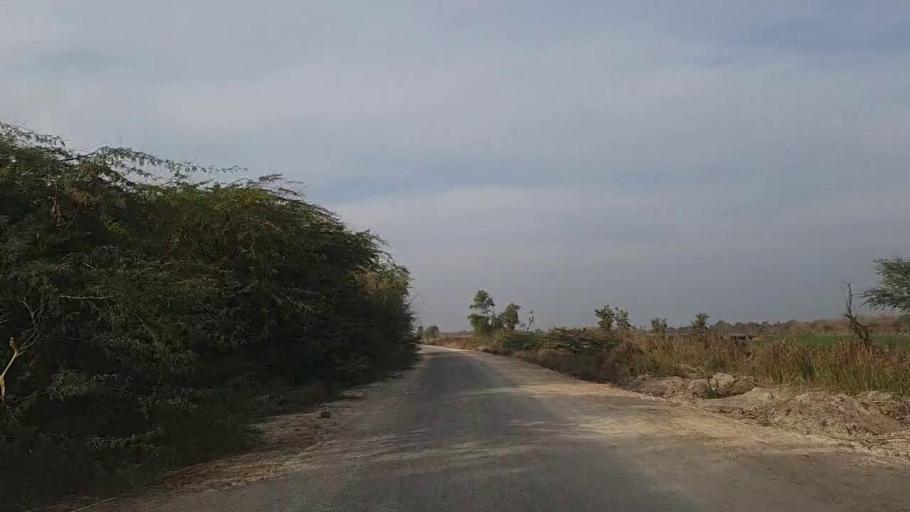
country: PK
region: Sindh
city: Daur
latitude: 26.4847
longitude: 68.4638
